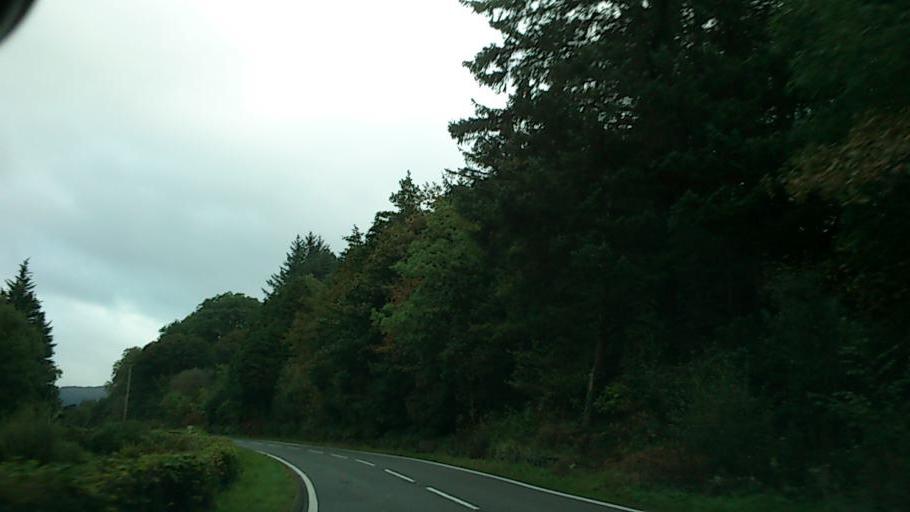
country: GB
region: Wales
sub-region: Sir Powys
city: Machynlleth
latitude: 52.5627
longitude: -3.9125
